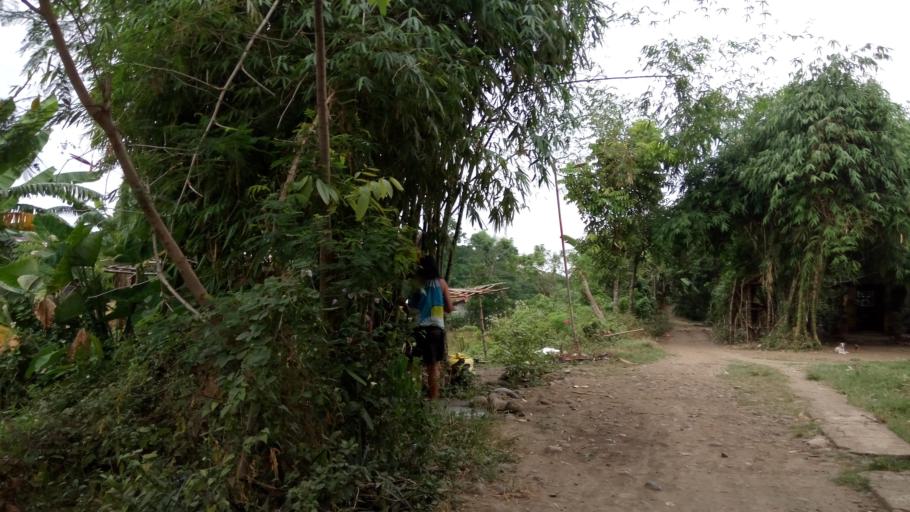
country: PH
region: Ilocos
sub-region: Province of La Union
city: Payocpoc Sur
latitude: 16.4656
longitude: 120.3330
